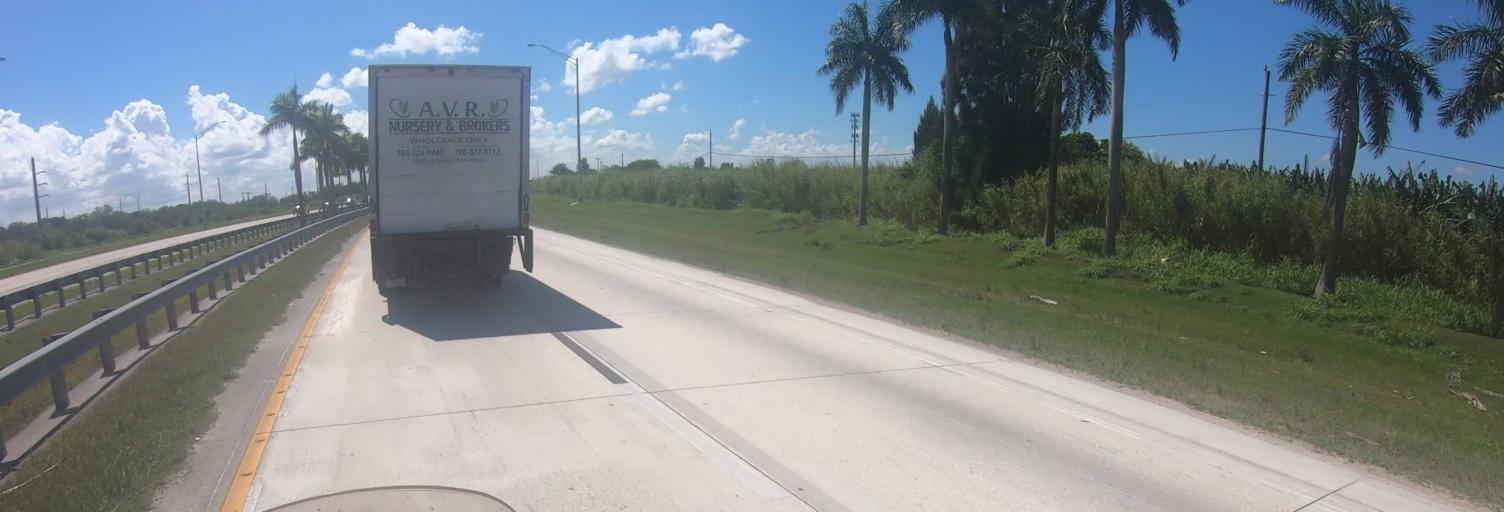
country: US
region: Florida
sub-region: Miami-Dade County
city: The Hammocks
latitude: 25.6857
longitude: -80.4791
